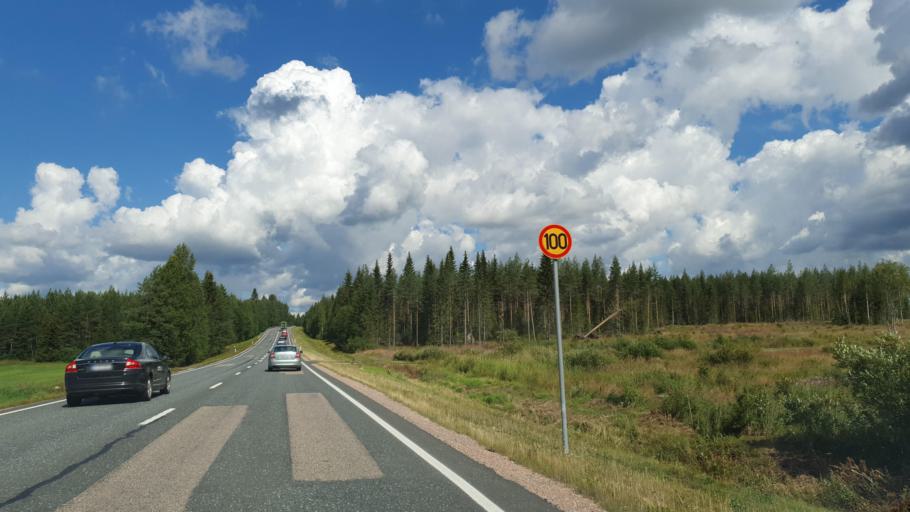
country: FI
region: Kainuu
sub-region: Kajaani
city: Kajaani
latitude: 64.0476
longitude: 27.4512
